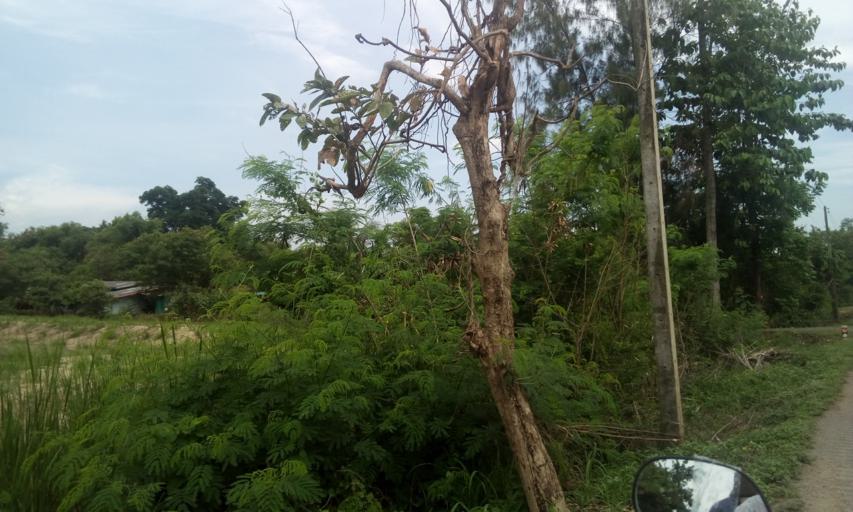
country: TH
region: Pathum Thani
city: Ban Lam Luk Ka
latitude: 13.9951
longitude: 100.8420
